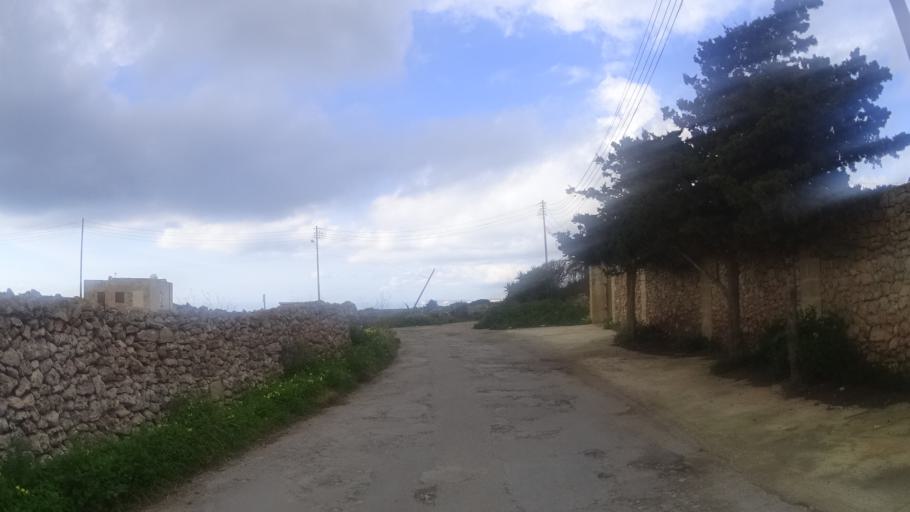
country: MT
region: L-Imgarr
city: Imgarr
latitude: 35.8976
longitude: 14.3652
